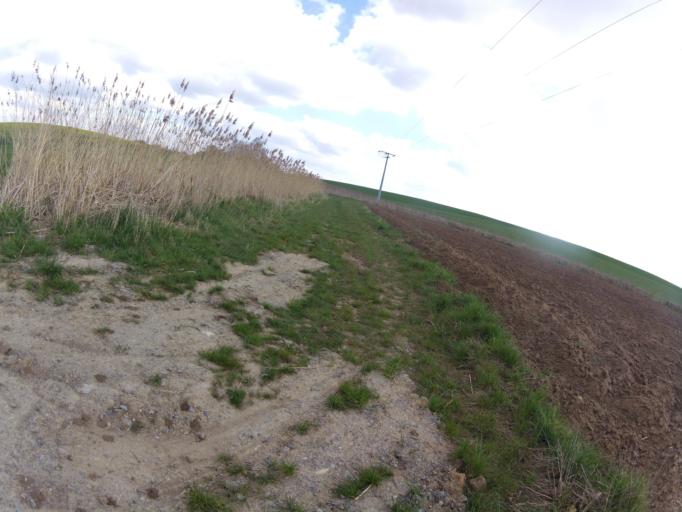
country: DE
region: Bavaria
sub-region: Regierungsbezirk Unterfranken
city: Sulzdorf
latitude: 49.6499
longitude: 9.9163
